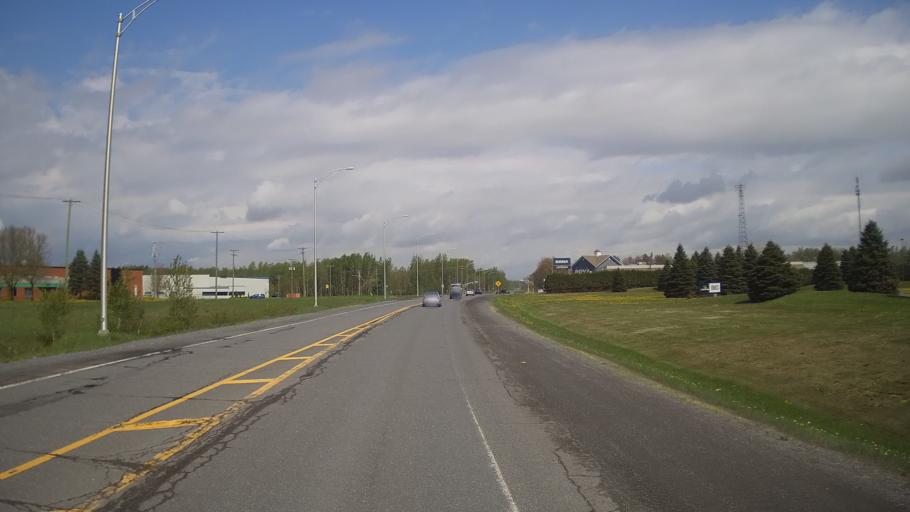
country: CA
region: Quebec
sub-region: Monteregie
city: Cowansville
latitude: 45.1950
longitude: -72.7616
